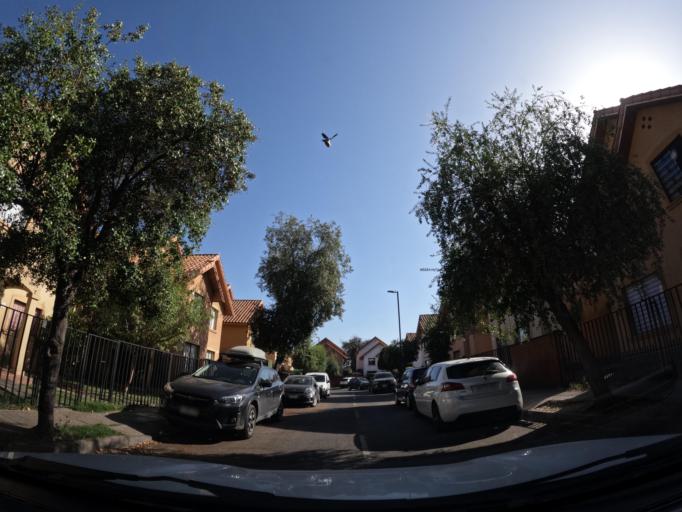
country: CL
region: Santiago Metropolitan
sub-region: Provincia de Santiago
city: Villa Presidente Frei, Nunoa, Santiago, Chile
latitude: -33.5100
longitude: -70.5451
